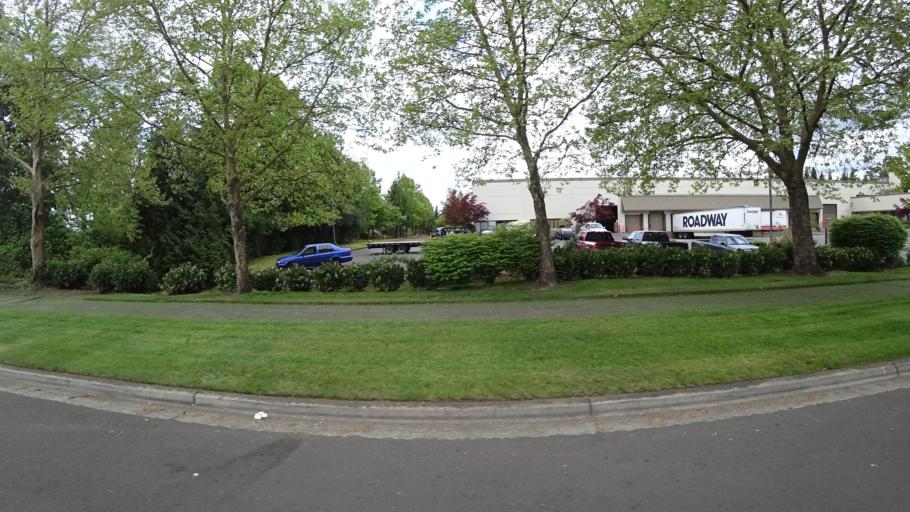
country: US
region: Oregon
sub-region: Washington County
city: Rockcreek
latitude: 45.5434
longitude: -122.8976
